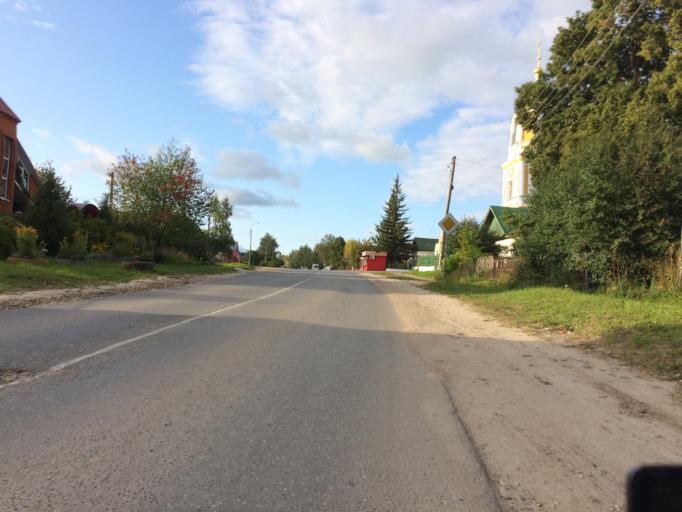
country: RU
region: Mariy-El
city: Yoshkar-Ola
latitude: 56.6498
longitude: 47.9805
